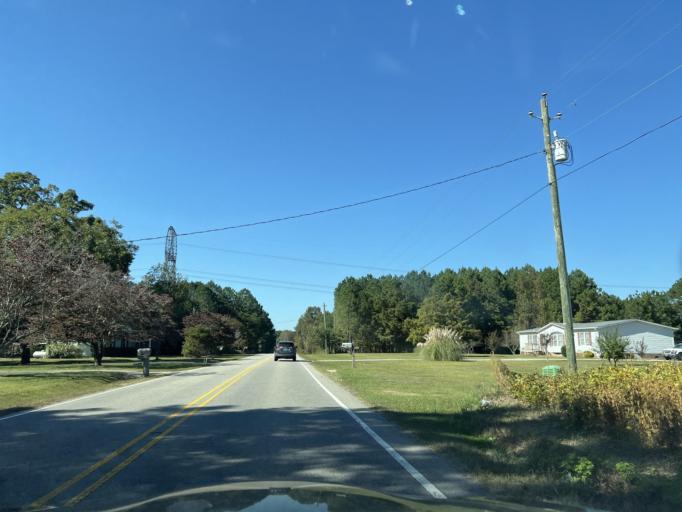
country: US
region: North Carolina
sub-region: Johnston County
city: Clayton
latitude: 35.6792
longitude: -78.5169
